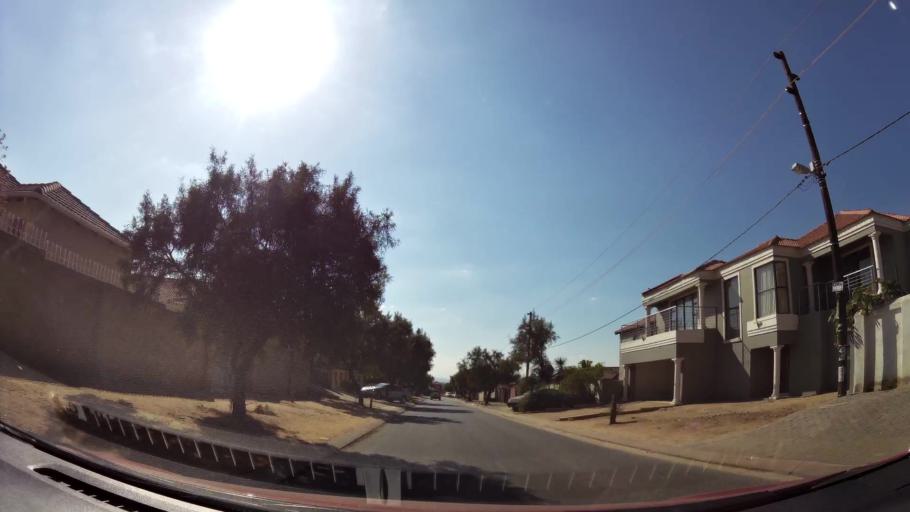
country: ZA
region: Gauteng
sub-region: West Rand District Municipality
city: Muldersdriseloop
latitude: -26.0211
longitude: 27.9393
